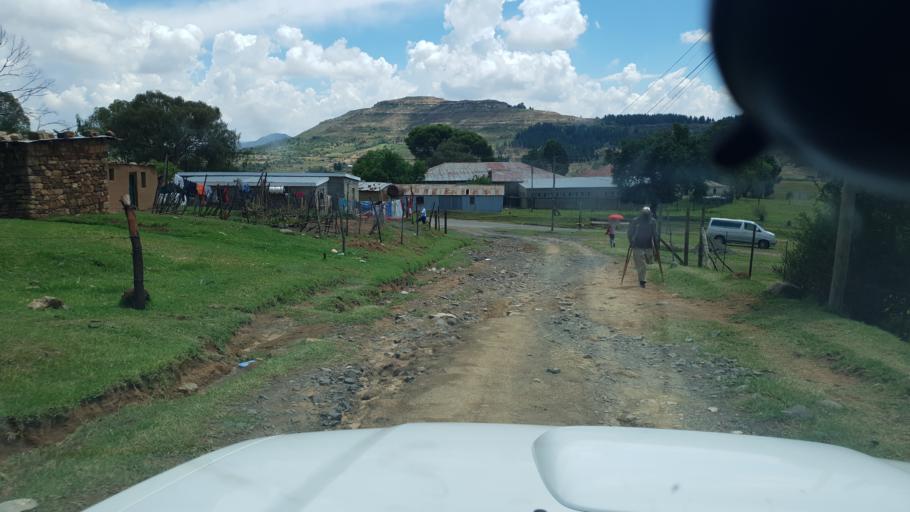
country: LS
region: Maseru
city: Nako
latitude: -29.6226
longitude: 27.5150
